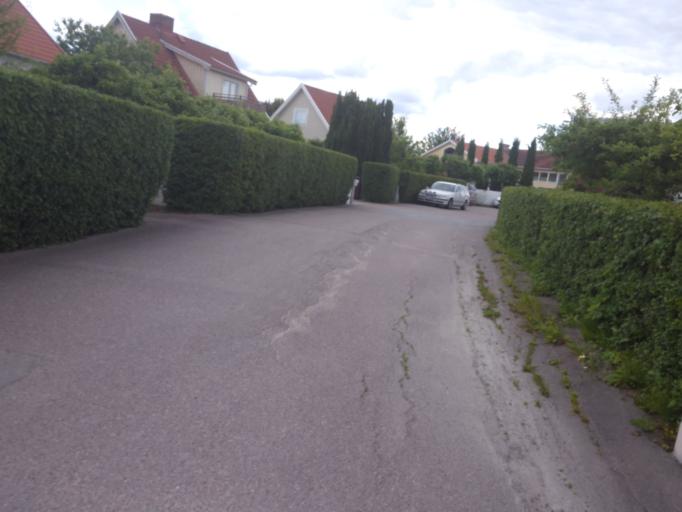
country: SE
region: Uppsala
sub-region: Uppsala Kommun
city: Uppsala
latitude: 59.8591
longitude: 17.6753
